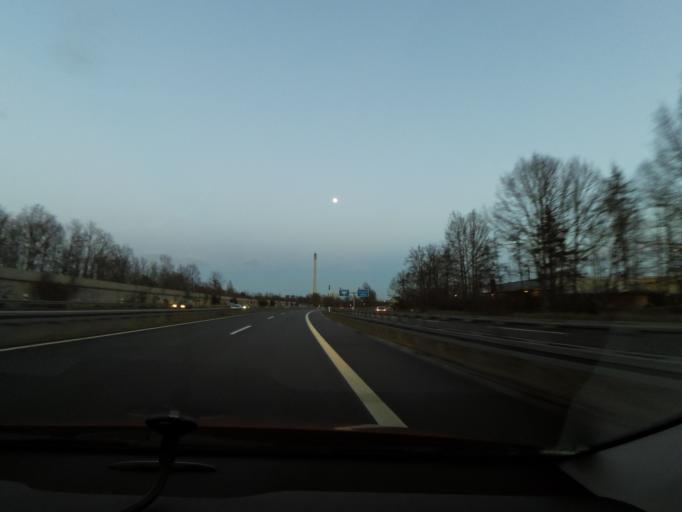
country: DE
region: Lower Saxony
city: Braunschweig
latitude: 52.2826
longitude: 10.4977
